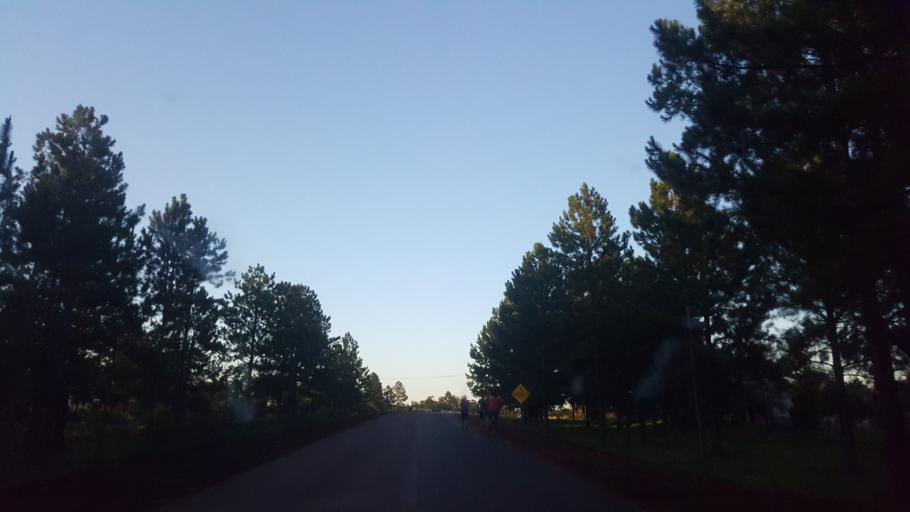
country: AR
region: Corrientes
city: Santo Tome
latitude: -28.5131
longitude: -56.0593
